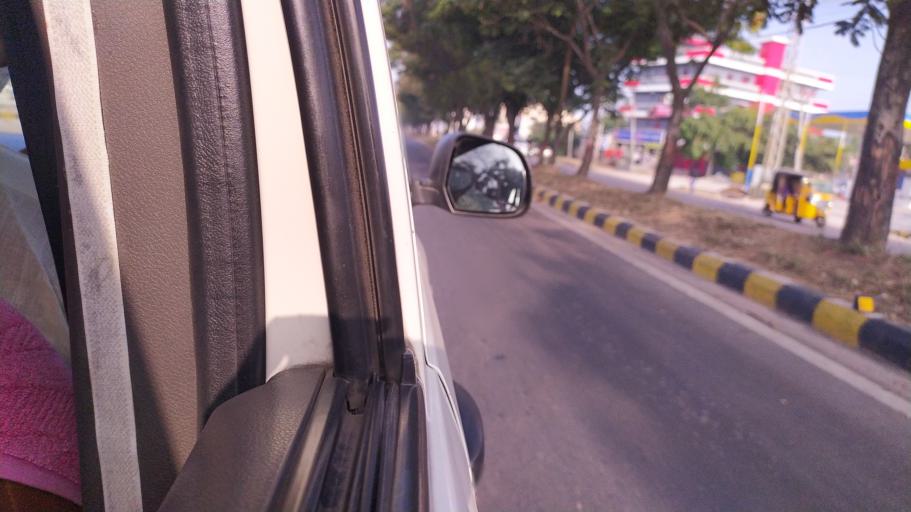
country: IN
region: Telangana
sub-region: Rangareddi
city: Balapur
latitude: 17.3147
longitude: 78.4434
